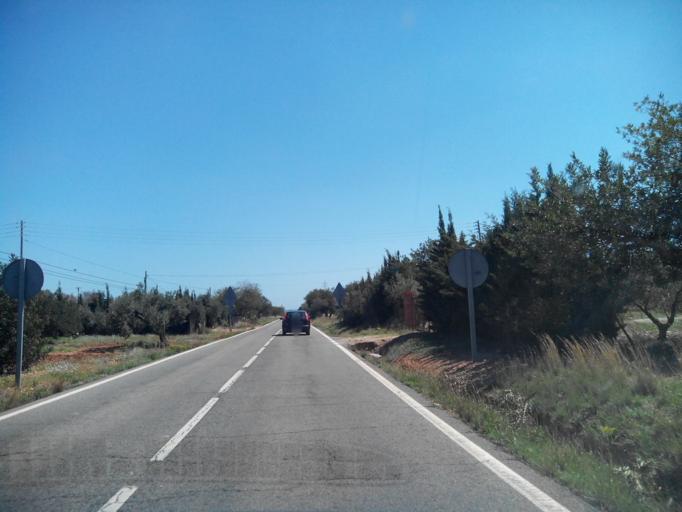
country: ES
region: Catalonia
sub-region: Provincia de Tarragona
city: Vilanova d'Escornalbou
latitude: 41.0804
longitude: 0.9634
